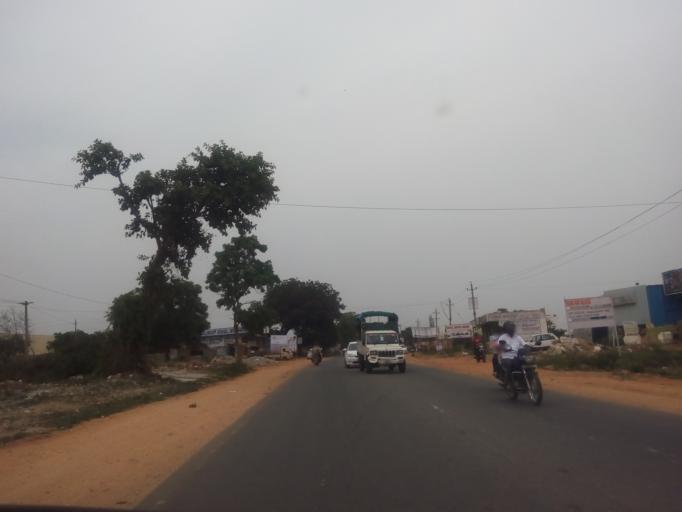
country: IN
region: Karnataka
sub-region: Bangalore Rural
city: Nelamangala
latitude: 12.9919
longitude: 77.4606
